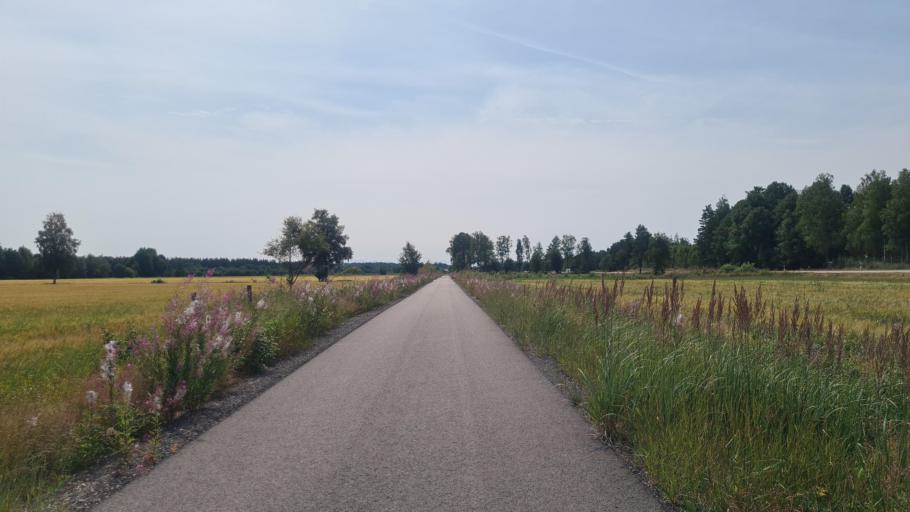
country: SE
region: Kronoberg
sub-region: Ljungby Kommun
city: Lagan
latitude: 56.8842
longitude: 13.9843
